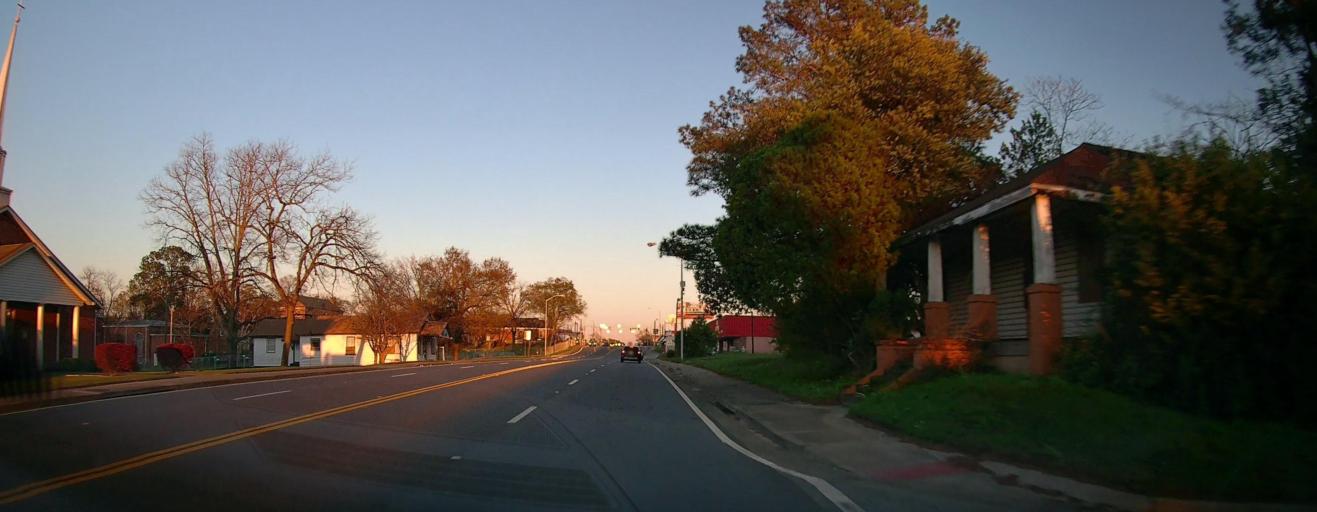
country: US
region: Georgia
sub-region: Crisp County
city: Cordele
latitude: 31.9635
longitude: -83.7910
